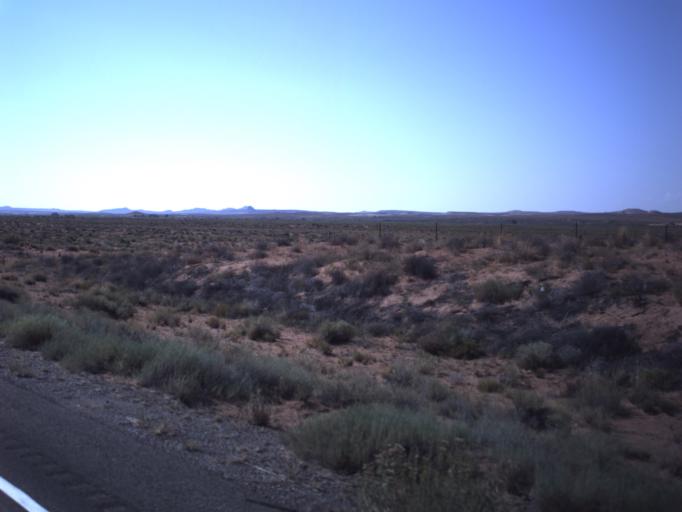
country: US
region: Utah
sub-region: San Juan County
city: Blanding
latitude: 37.1386
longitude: -109.5569
